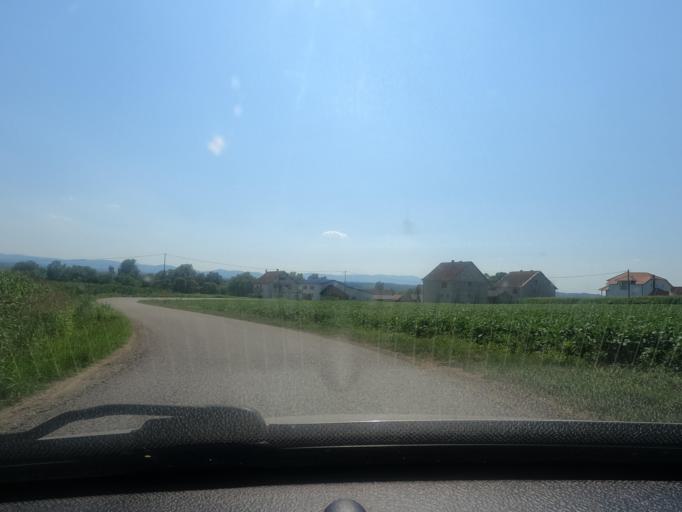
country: RS
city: Jarebice
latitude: 44.5368
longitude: 19.3747
